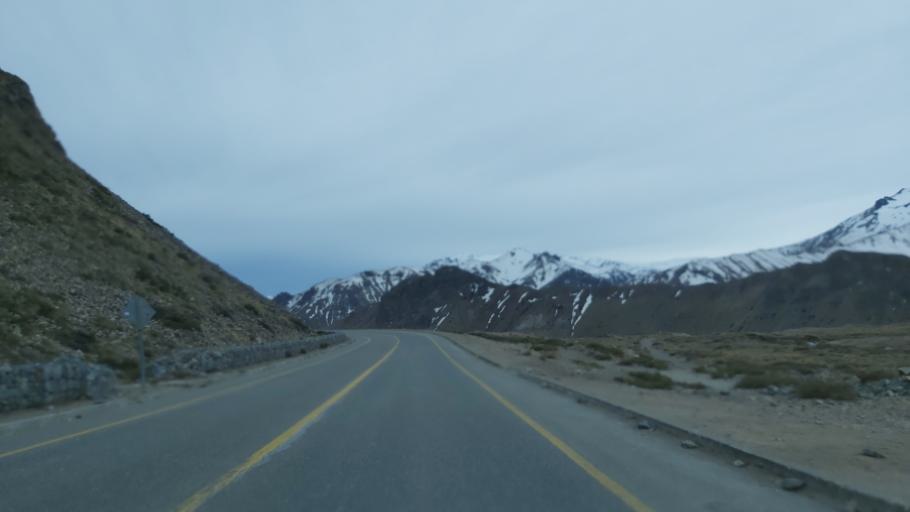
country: CL
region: Maule
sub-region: Provincia de Linares
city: Colbun
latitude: -35.9587
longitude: -70.5733
